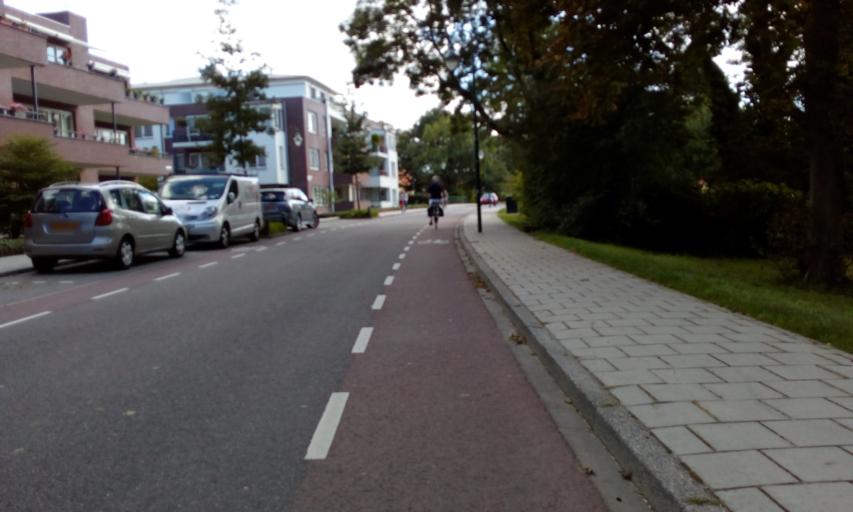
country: NL
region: South Holland
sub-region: Gemeente Leiden
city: Leiden
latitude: 52.1196
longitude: 4.4963
